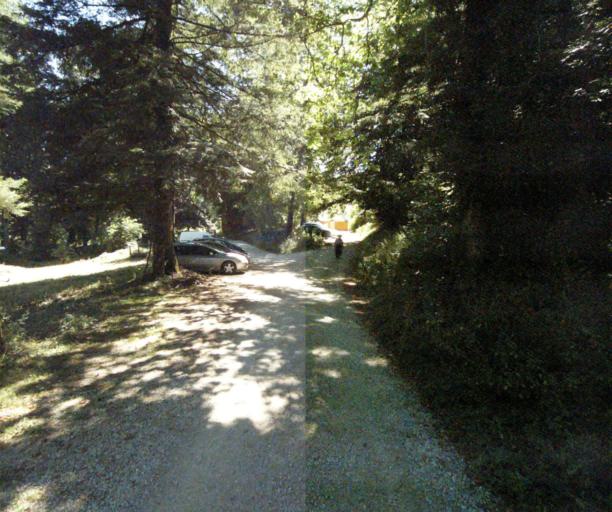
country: FR
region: Midi-Pyrenees
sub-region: Departement du Tarn
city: Dourgne
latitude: 43.4382
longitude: 2.1292
